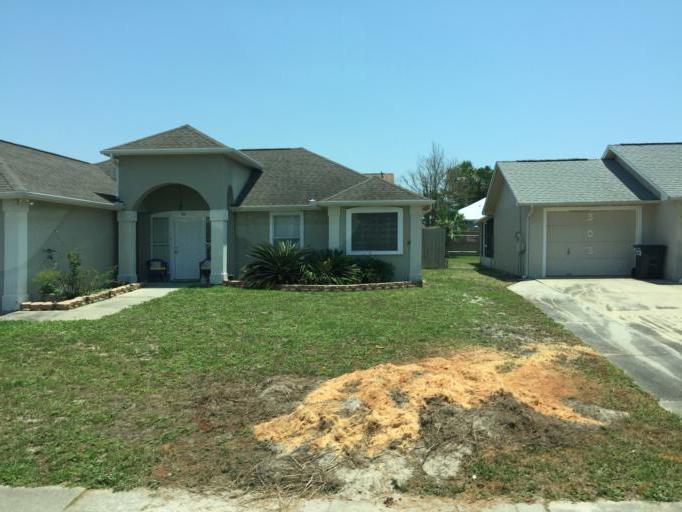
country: US
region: Florida
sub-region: Bay County
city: Panama City Beach
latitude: 30.2072
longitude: -85.8515
